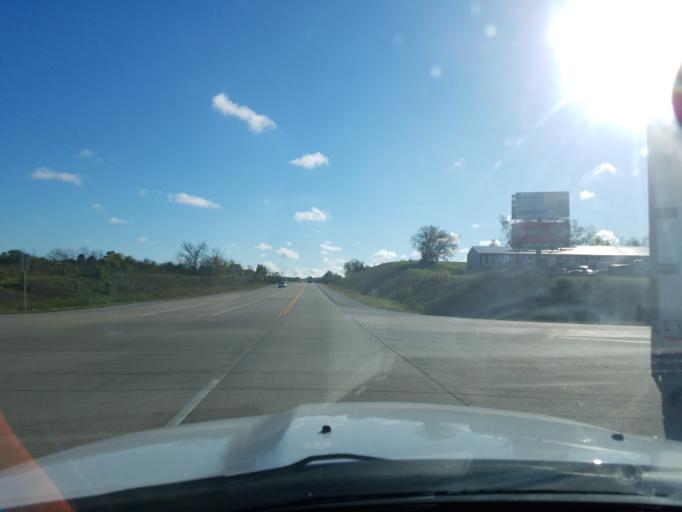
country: US
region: Kentucky
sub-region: Washington County
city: Springfield
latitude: 37.7065
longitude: -85.2347
